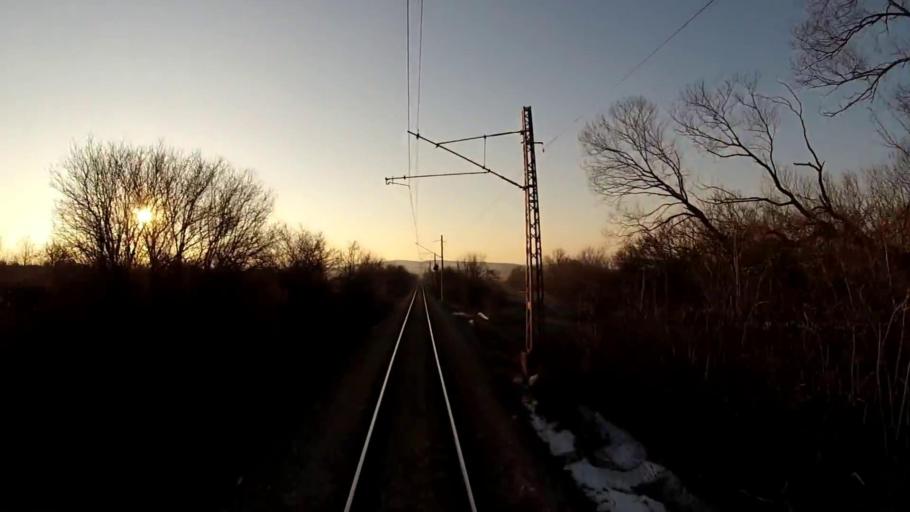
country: BG
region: Sofiya
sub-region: Obshtina Slivnitsa
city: Slivnitsa
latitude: 42.8822
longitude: 22.9828
